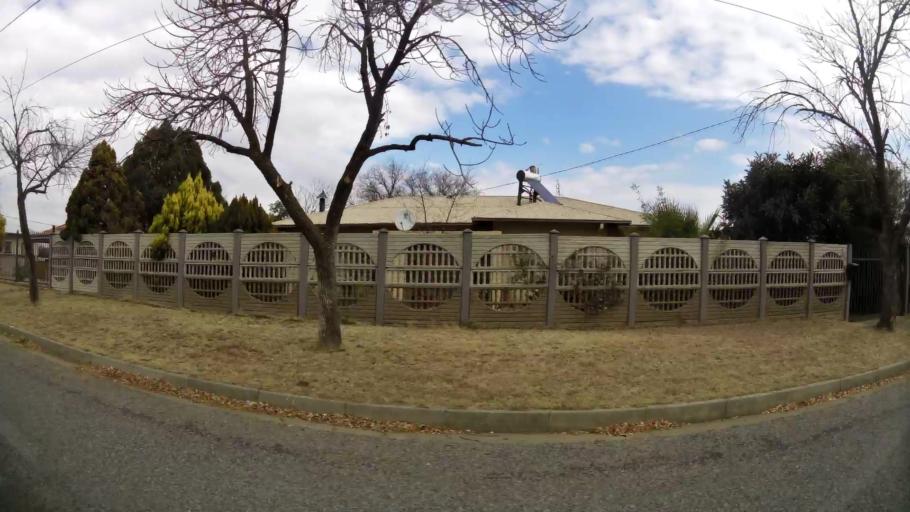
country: ZA
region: Orange Free State
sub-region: Fezile Dabi District Municipality
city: Kroonstad
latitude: -27.6497
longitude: 27.2332
